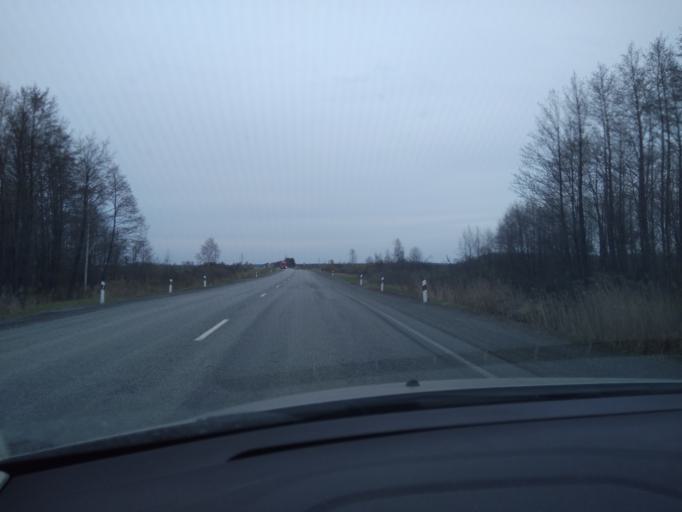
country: RU
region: Sverdlovsk
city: Pyshma
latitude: 57.0232
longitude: 63.3984
